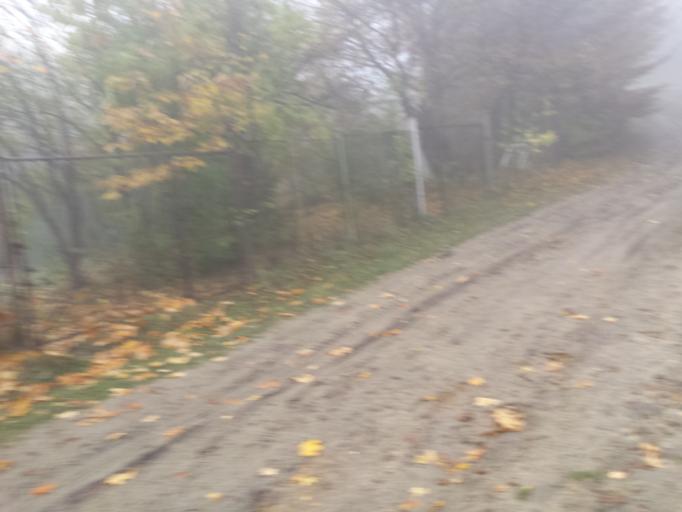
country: RO
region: Cluj
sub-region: Comuna Baciu
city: Baciu
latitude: 46.7691
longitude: 23.5389
